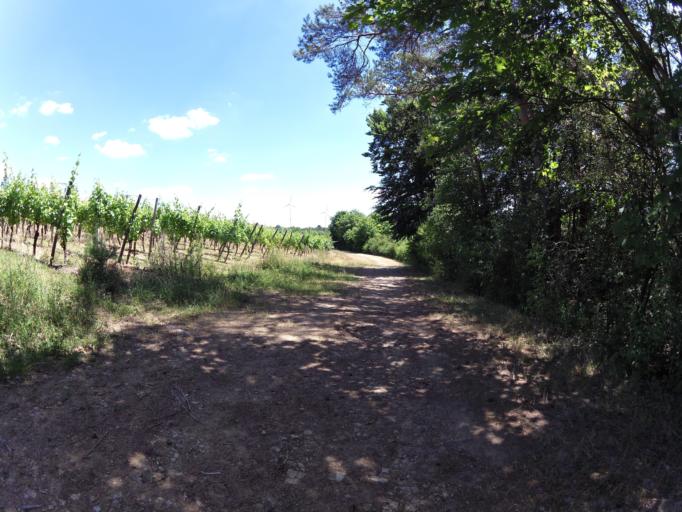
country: DE
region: Bavaria
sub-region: Regierungsbezirk Unterfranken
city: Thungersheim
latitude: 49.8897
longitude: 9.8601
